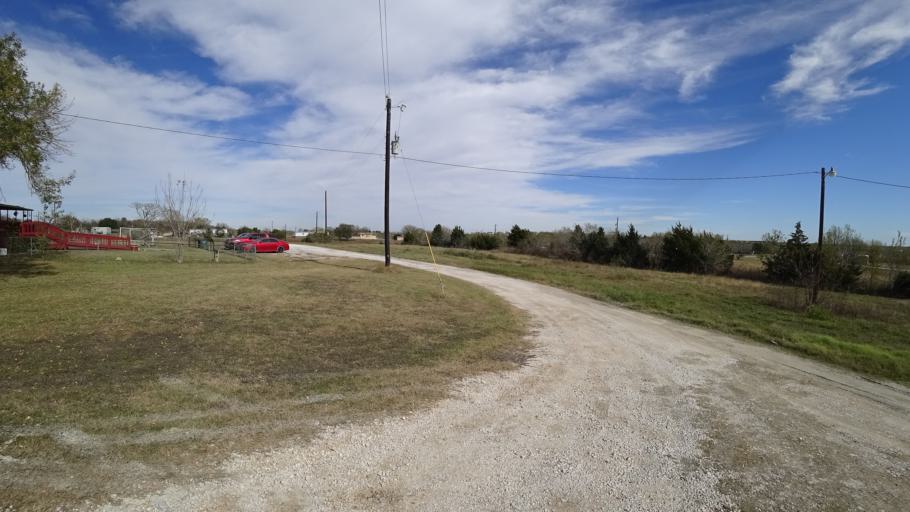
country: US
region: Texas
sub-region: Travis County
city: Onion Creek
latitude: 30.1161
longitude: -97.7306
